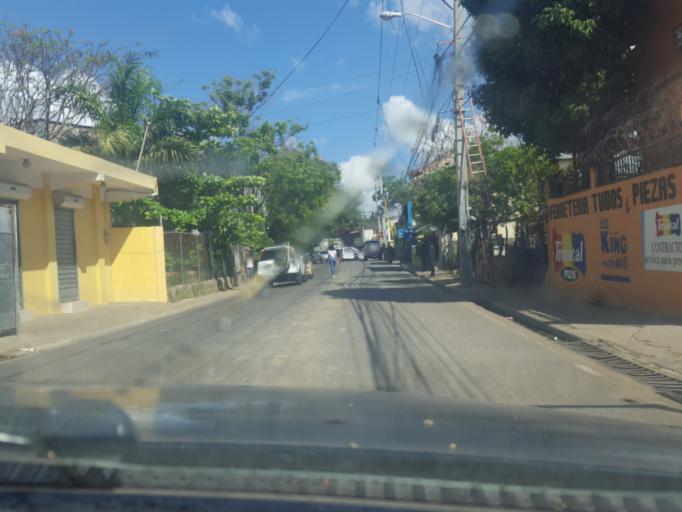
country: DO
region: Santiago
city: Santiago de los Caballeros
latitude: 19.4875
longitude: -70.7028
